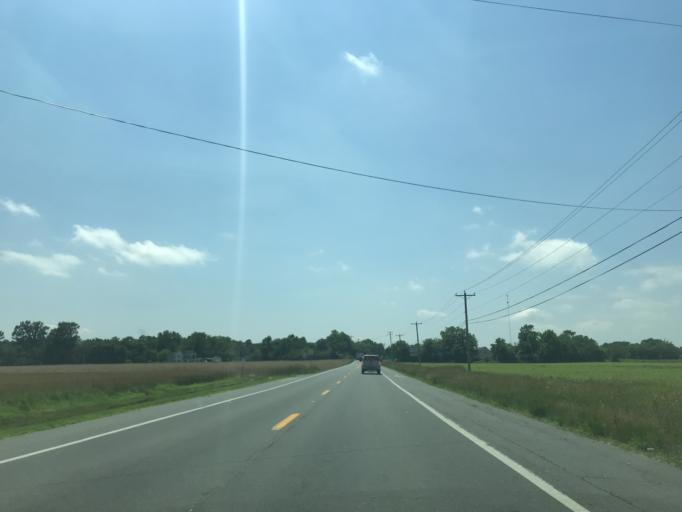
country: US
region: Maryland
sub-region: Dorchester County
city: Hurlock
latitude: 38.5972
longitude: -75.9101
